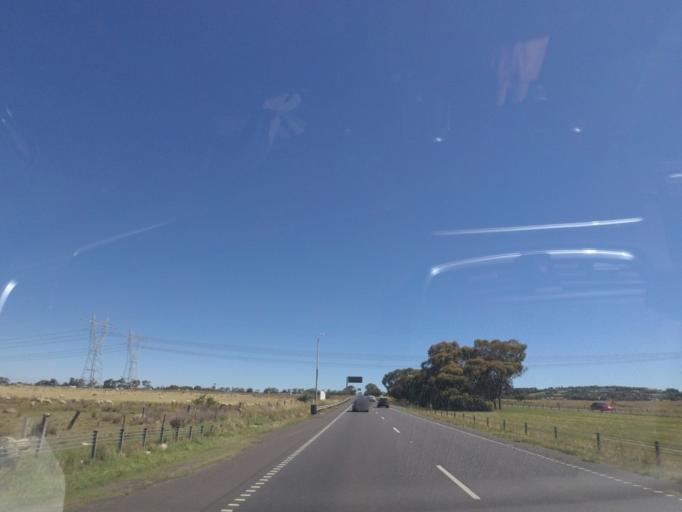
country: AU
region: Victoria
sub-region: Hume
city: Craigieburn
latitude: -37.5530
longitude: 144.9436
